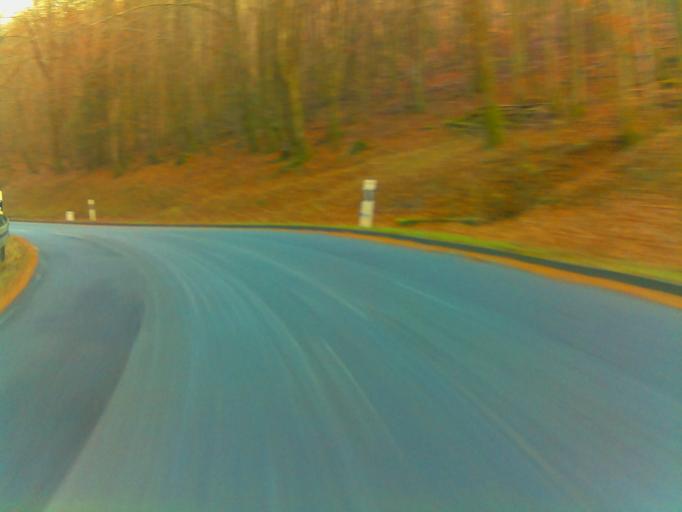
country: DE
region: Hesse
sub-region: Regierungsbezirk Darmstadt
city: Hesseneck
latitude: 49.5407
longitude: 9.0887
